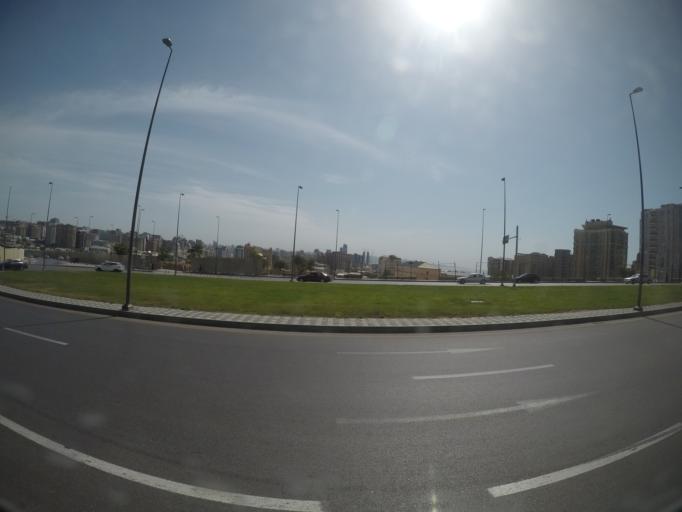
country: AZ
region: Baki
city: Badamdar
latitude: 40.3708
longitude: 49.8246
